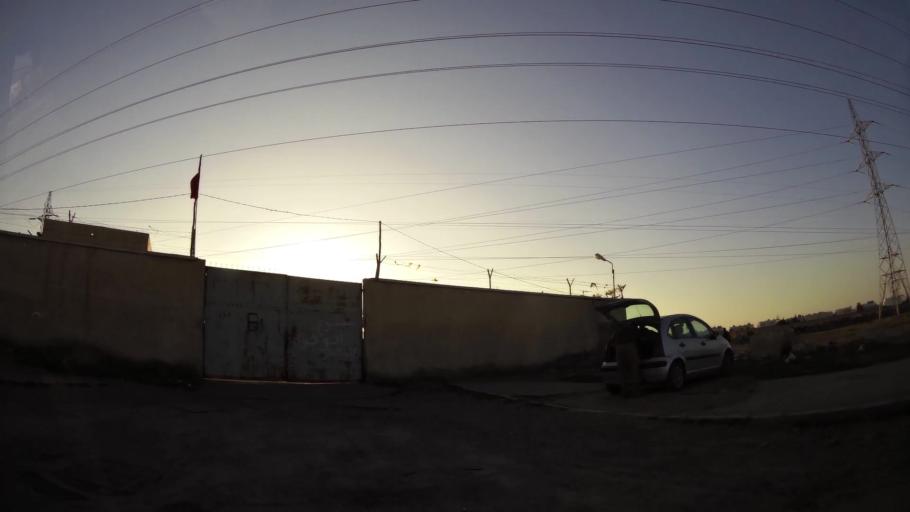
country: MA
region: Oriental
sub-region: Oujda-Angad
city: Oujda
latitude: 34.7118
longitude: -1.9145
